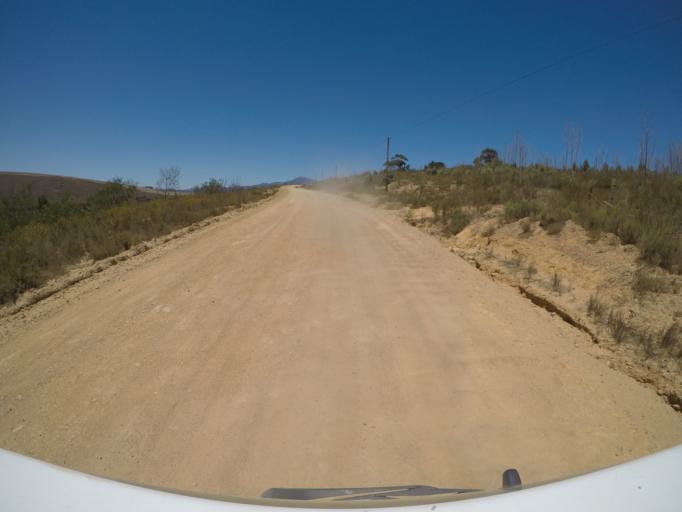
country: ZA
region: Western Cape
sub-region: Overberg District Municipality
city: Grabouw
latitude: -34.2193
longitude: 19.2041
